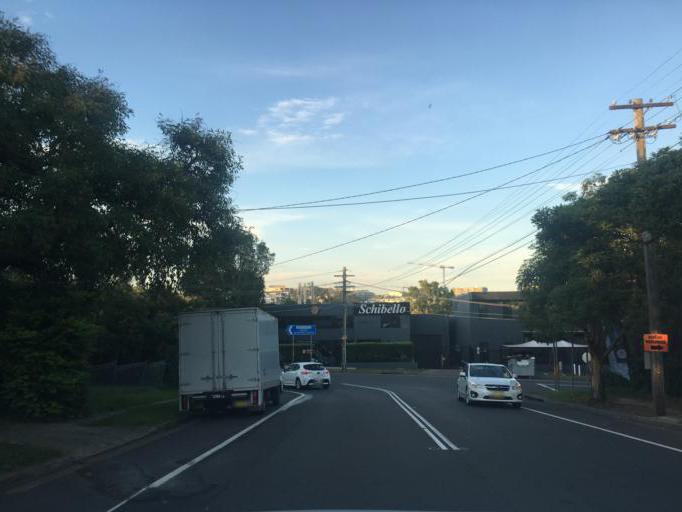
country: AU
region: New South Wales
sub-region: Canada Bay
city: Rhodes
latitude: -33.8249
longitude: 151.0899
